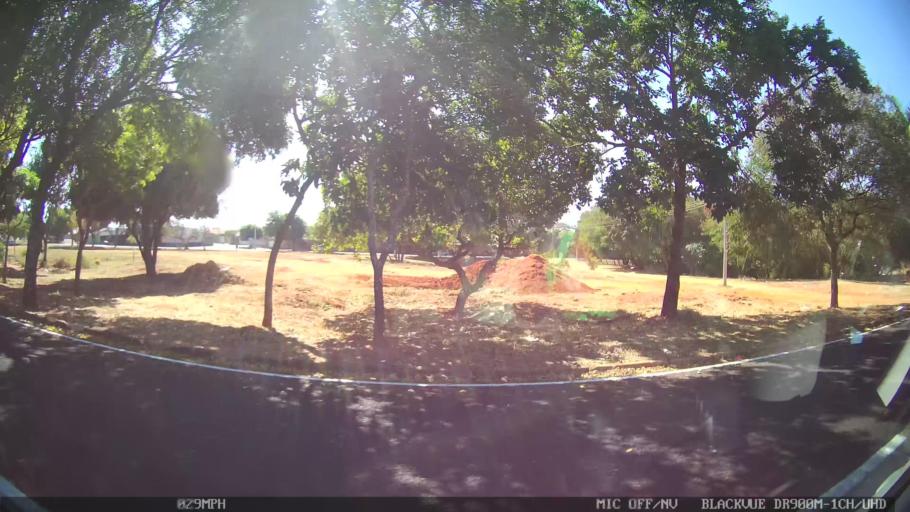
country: BR
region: Sao Paulo
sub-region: Sao Jose Do Rio Preto
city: Sao Jose do Rio Preto
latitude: -20.7741
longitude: -49.4109
